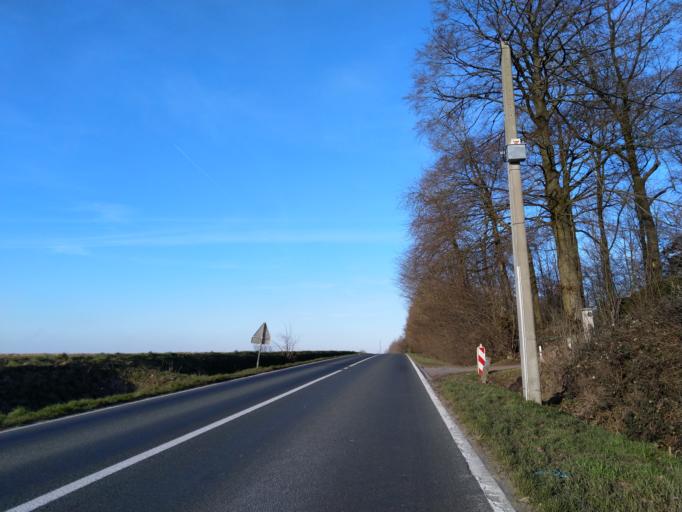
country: BE
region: Wallonia
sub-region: Province du Hainaut
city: Frameries
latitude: 50.3694
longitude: 3.8938
